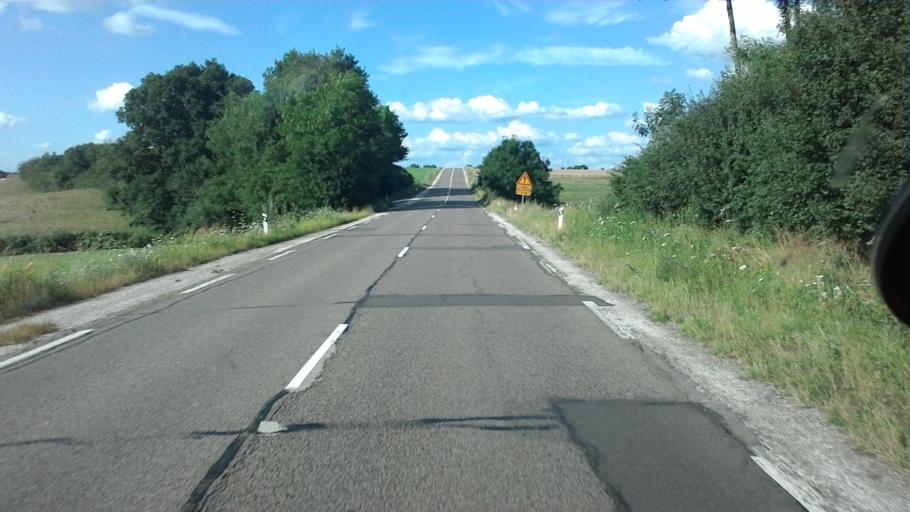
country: FR
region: Franche-Comte
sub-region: Departement de la Haute-Saone
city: Luxeuil-les-Bains
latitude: 47.7133
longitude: 6.2988
